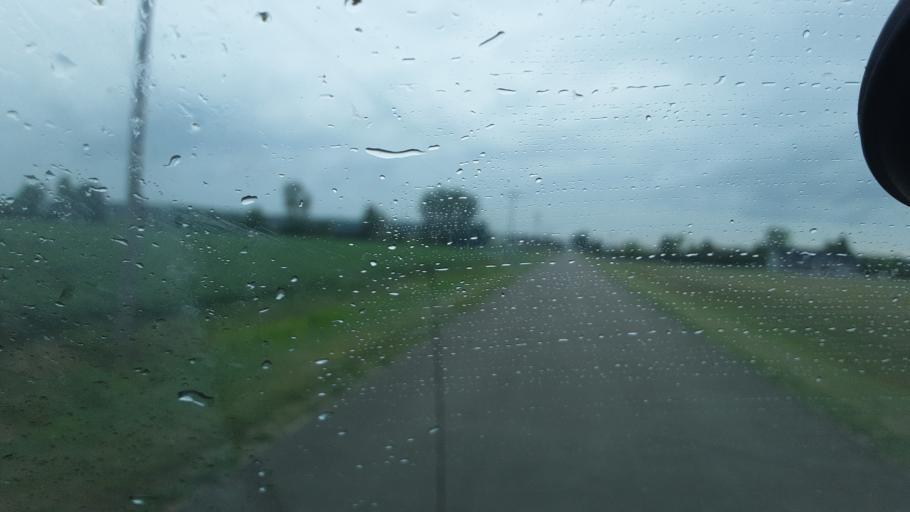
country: US
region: Ohio
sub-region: Defiance County
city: Hicksville
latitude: 41.2998
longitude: -84.6697
